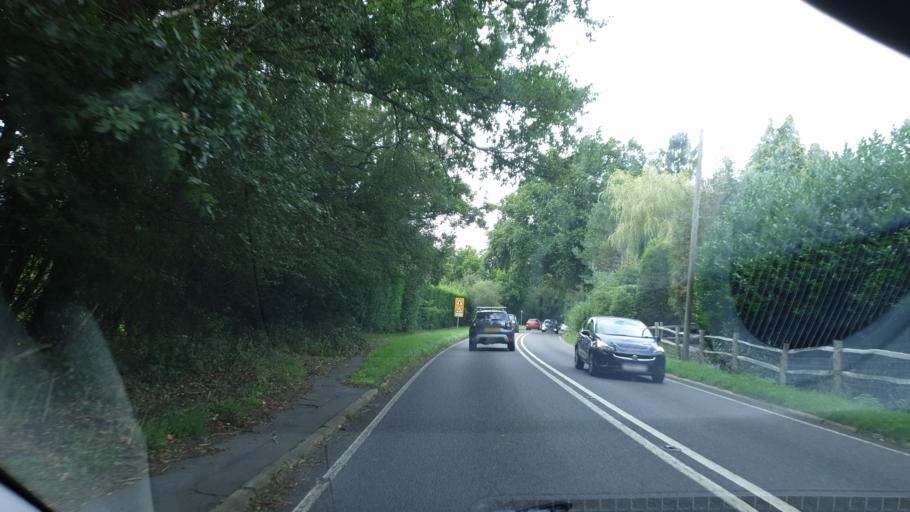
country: GB
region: England
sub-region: East Sussex
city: Forest Row
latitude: 51.1099
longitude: 0.0237
